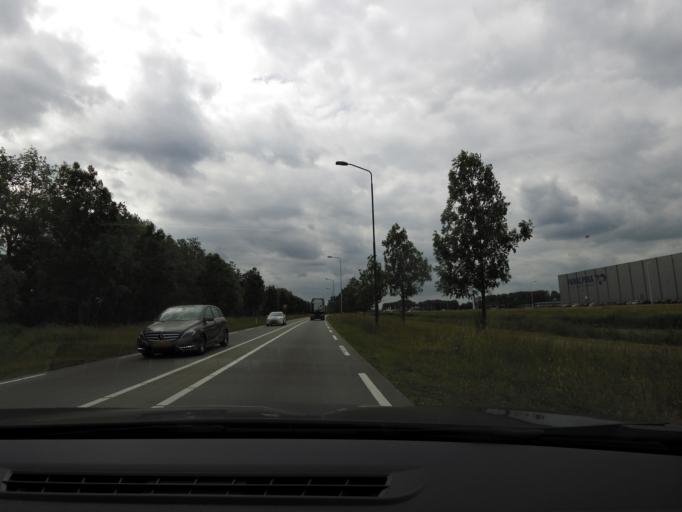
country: NL
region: North Brabant
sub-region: Gemeente Moerdijk
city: Klundert
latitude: 51.6538
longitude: 4.5634
